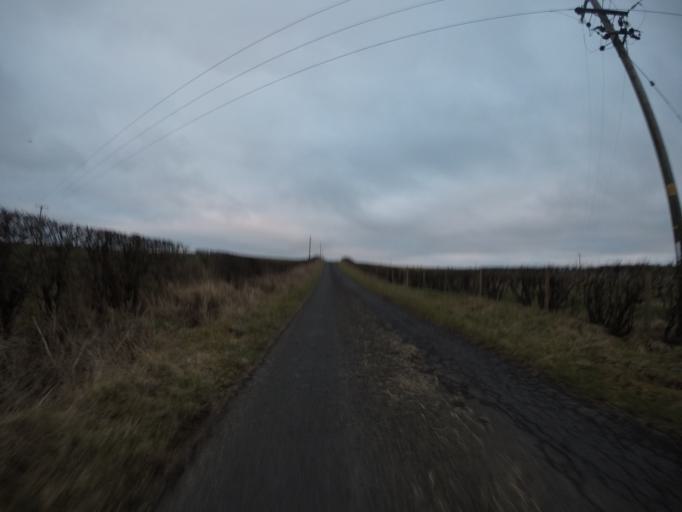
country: GB
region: Scotland
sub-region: North Ayrshire
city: Dalry
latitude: 55.6864
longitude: -4.7608
